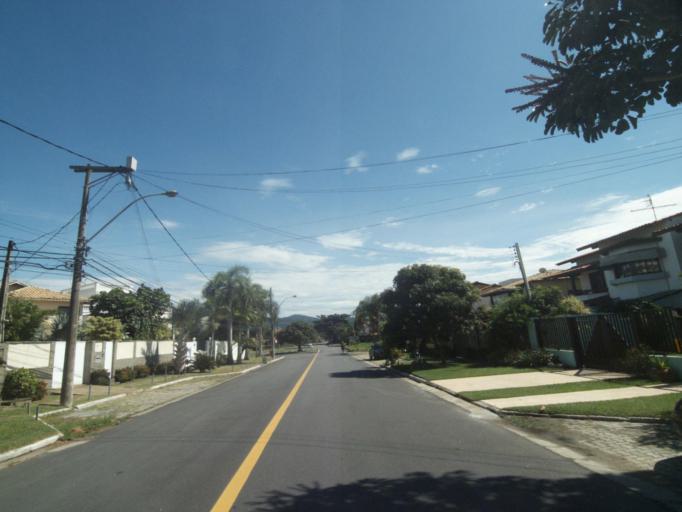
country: BR
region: Rio de Janeiro
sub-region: Niteroi
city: Niteroi
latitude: -22.9600
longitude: -43.0562
